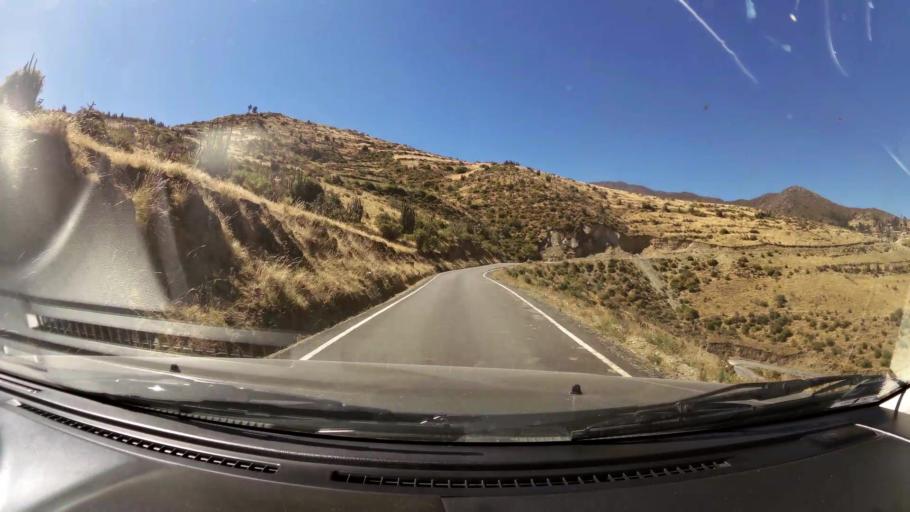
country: PE
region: Huancavelica
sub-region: Huaytara
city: Quito-Arma
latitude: -13.6851
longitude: -75.3859
